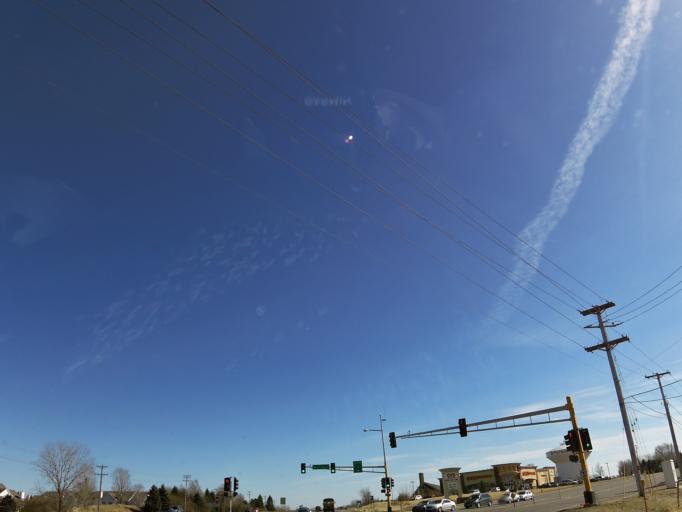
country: US
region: Minnesota
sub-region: Hennepin County
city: Plymouth
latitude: 45.0322
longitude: -93.5079
